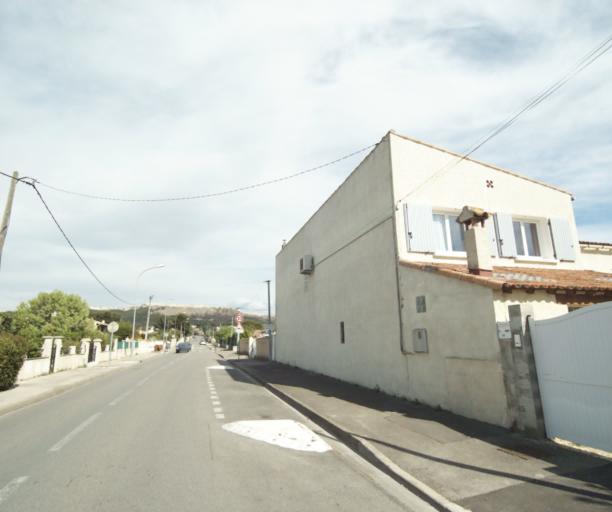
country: FR
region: Provence-Alpes-Cote d'Azur
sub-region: Departement des Bouches-du-Rhone
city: Rognac
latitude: 43.4921
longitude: 5.2221
